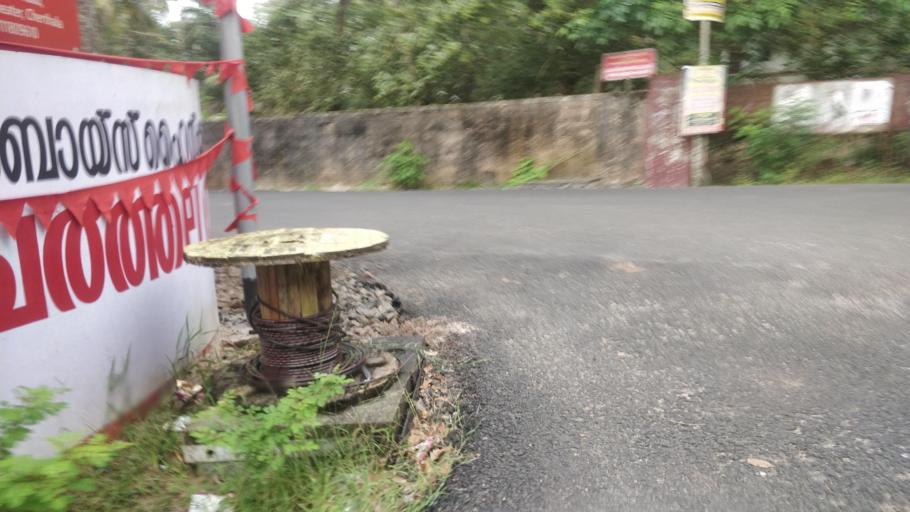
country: IN
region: Kerala
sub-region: Alappuzha
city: Shertallai
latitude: 9.6779
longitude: 76.3508
